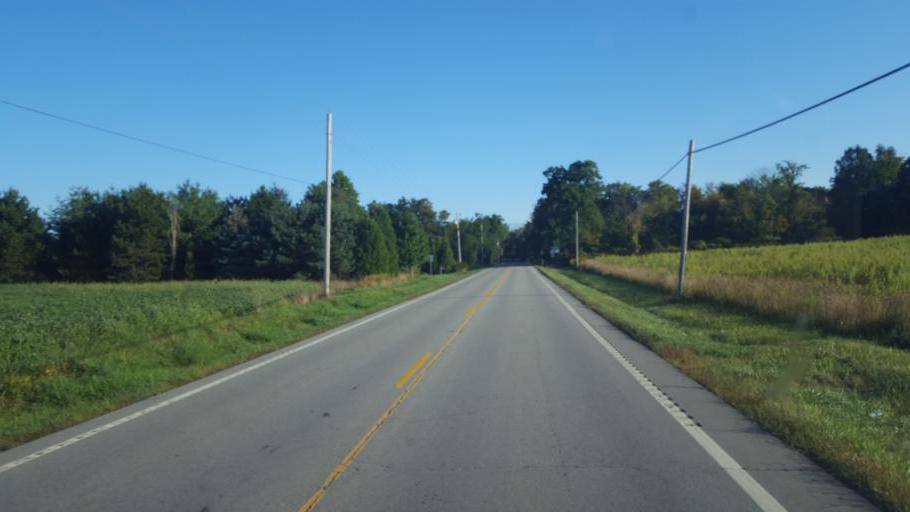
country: US
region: Ohio
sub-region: Lorain County
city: Wellington
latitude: 41.1179
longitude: -82.3035
